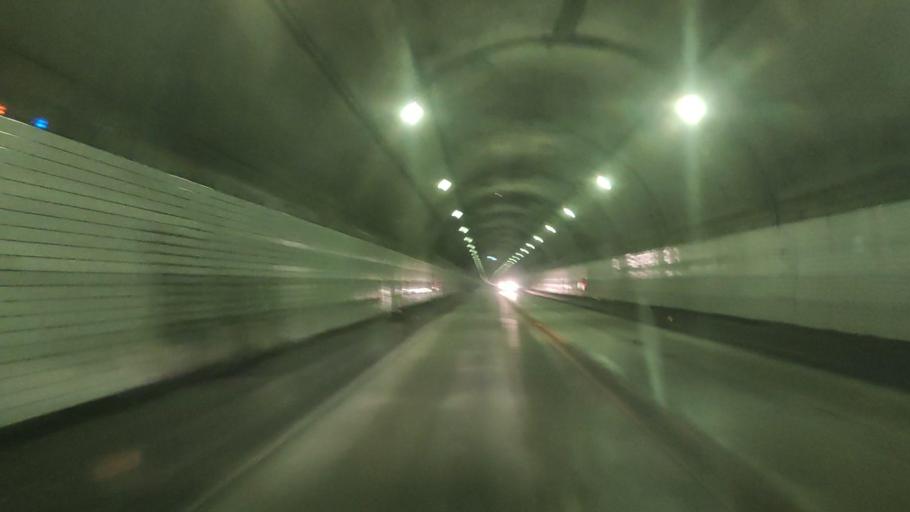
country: JP
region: Fukuoka
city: Maebaru-chuo
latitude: 33.4712
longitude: 130.2829
